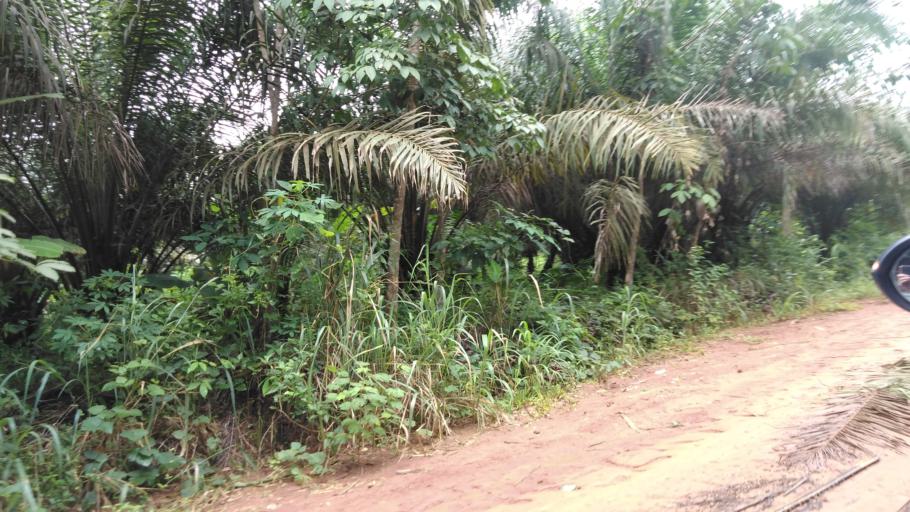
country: NG
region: Ogun
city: Abigi
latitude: 6.5845
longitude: 4.5578
